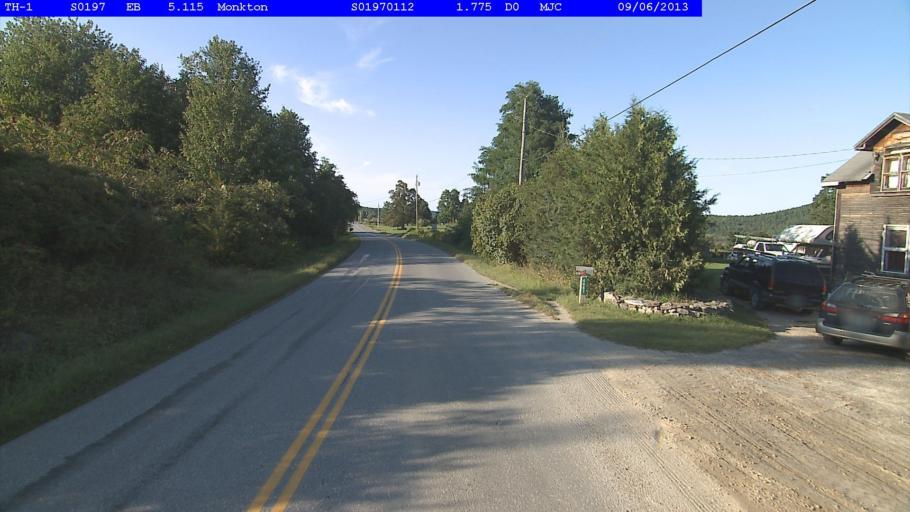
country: US
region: Vermont
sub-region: Addison County
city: Vergennes
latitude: 44.2081
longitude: -73.1631
